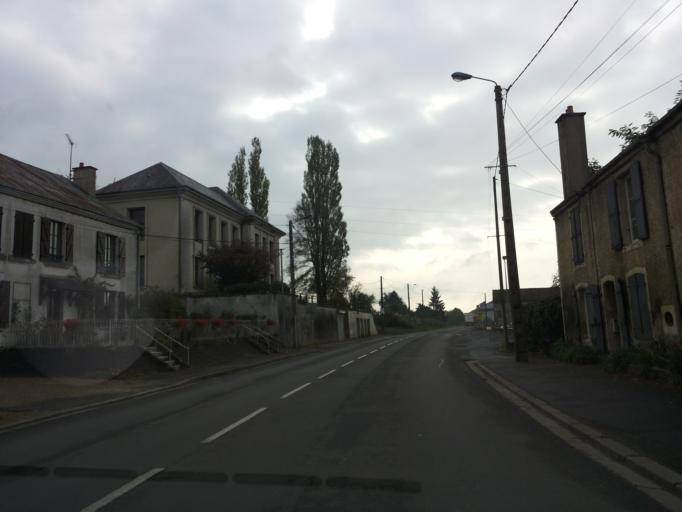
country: FR
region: Champagne-Ardenne
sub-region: Departement des Ardennes
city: Blagny
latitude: 49.6196
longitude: 5.1910
